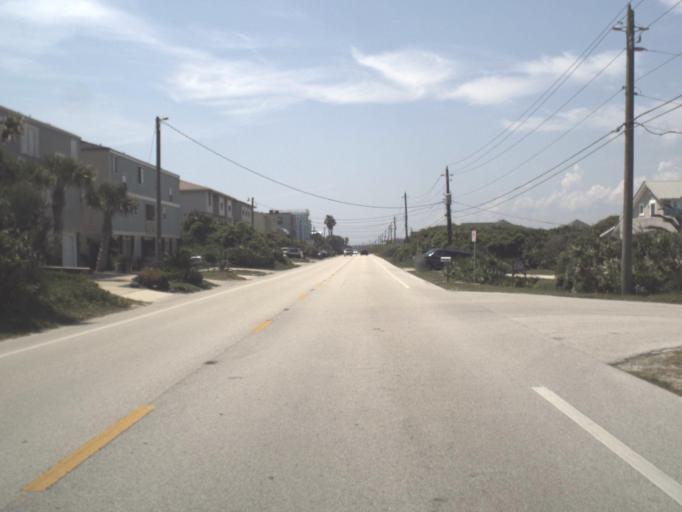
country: US
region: Florida
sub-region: Saint Johns County
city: Villano Beach
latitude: 29.9483
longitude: -81.3033
